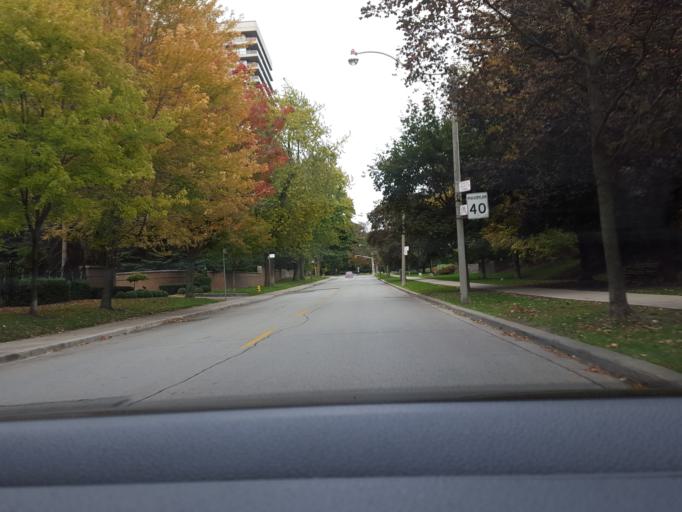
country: CA
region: Ontario
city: Toronto
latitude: 43.6867
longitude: -79.3905
